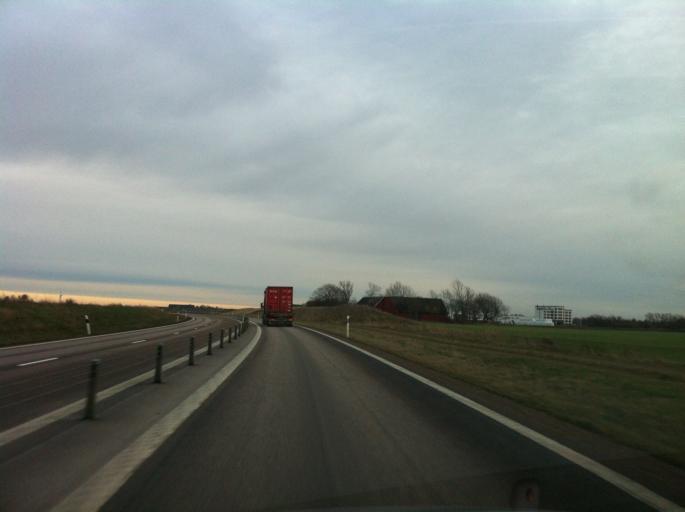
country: SE
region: Skane
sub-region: Hoganas Kommun
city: Hoganas
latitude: 56.1658
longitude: 12.5737
